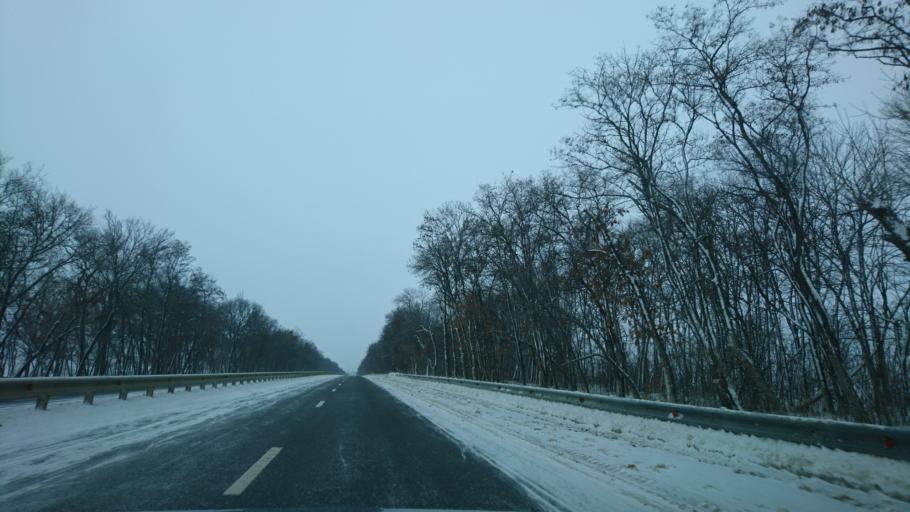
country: RU
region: Belgorod
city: Bessonovka
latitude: 50.3633
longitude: 36.3143
